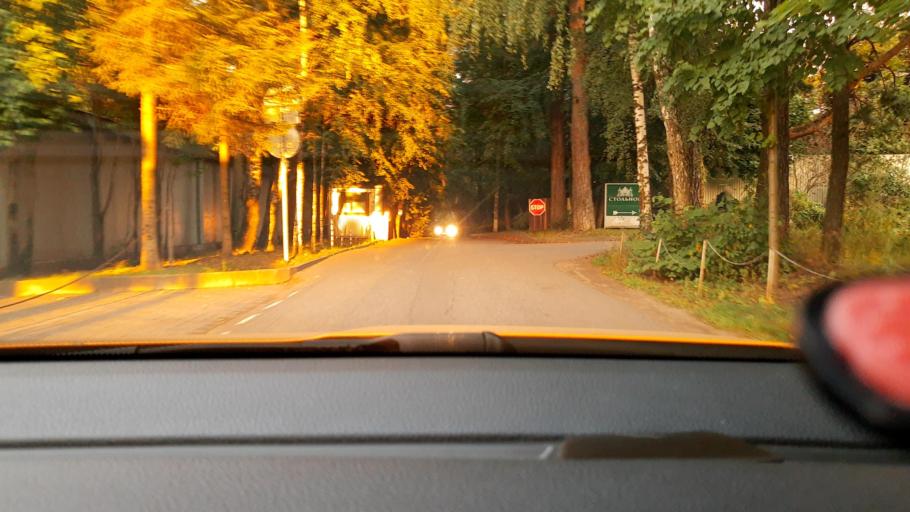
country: RU
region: Moscow
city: Novo-Peredelkino
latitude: 55.6670
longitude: 37.3356
